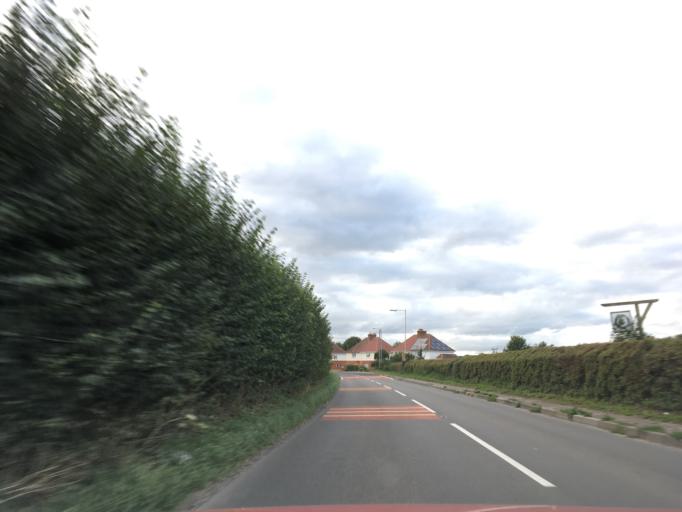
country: GB
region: England
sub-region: Wiltshire
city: Devizes
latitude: 51.3617
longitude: -2.0181
